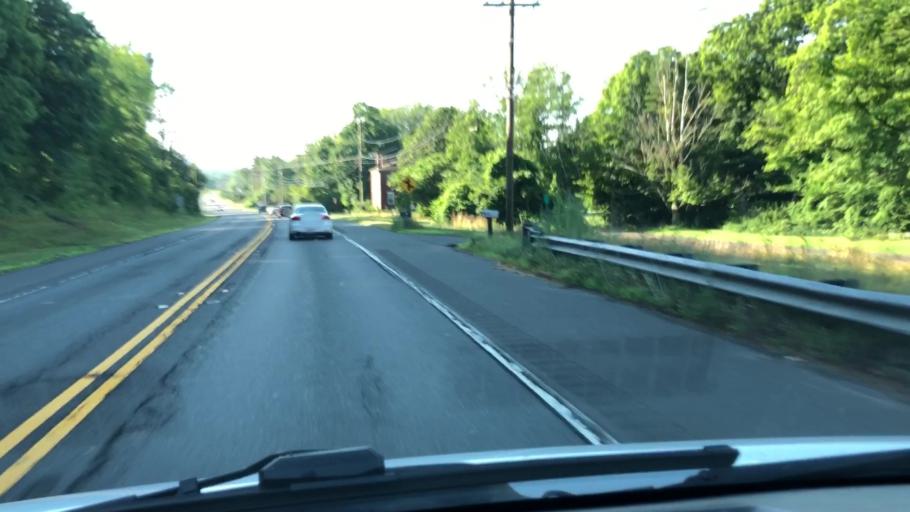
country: US
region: Massachusetts
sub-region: Hampshire County
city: North Amherst
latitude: 42.4333
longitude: -72.5457
